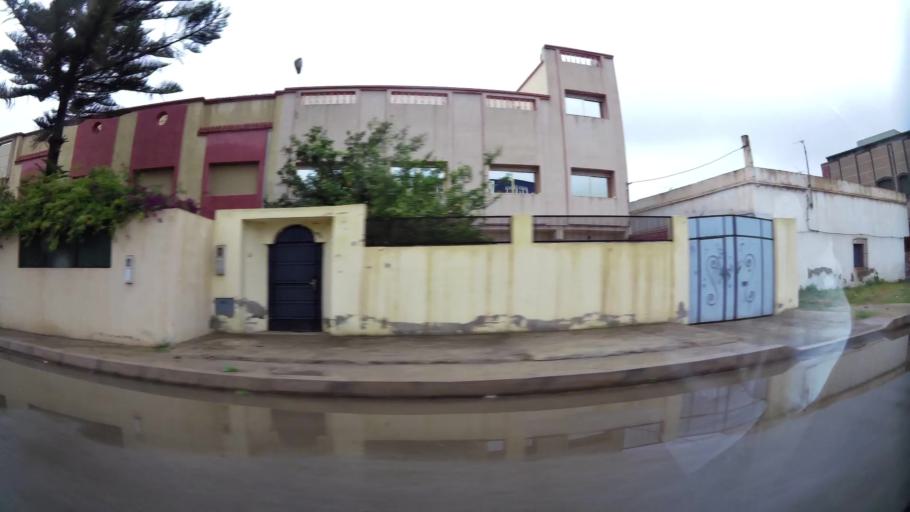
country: MA
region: Oriental
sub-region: Nador
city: Nador
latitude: 35.1587
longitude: -2.9699
